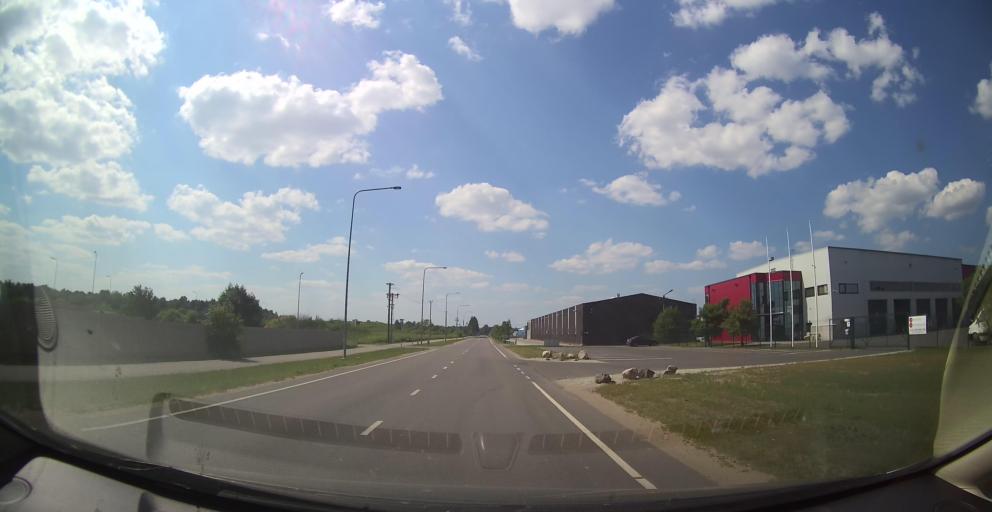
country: EE
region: Harju
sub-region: Joelaehtme vald
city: Loo
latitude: 59.4307
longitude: 24.9702
